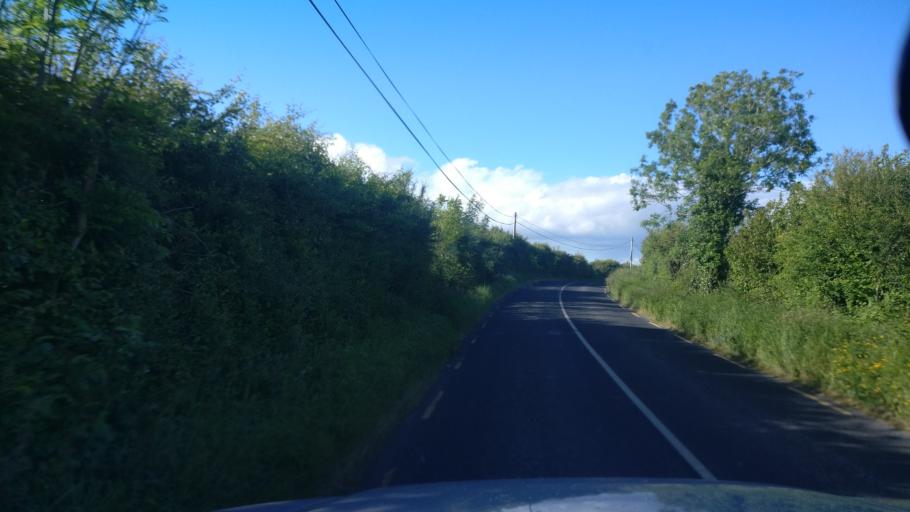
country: IE
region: Connaught
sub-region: County Galway
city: Ballinasloe
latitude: 53.2101
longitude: -8.2973
